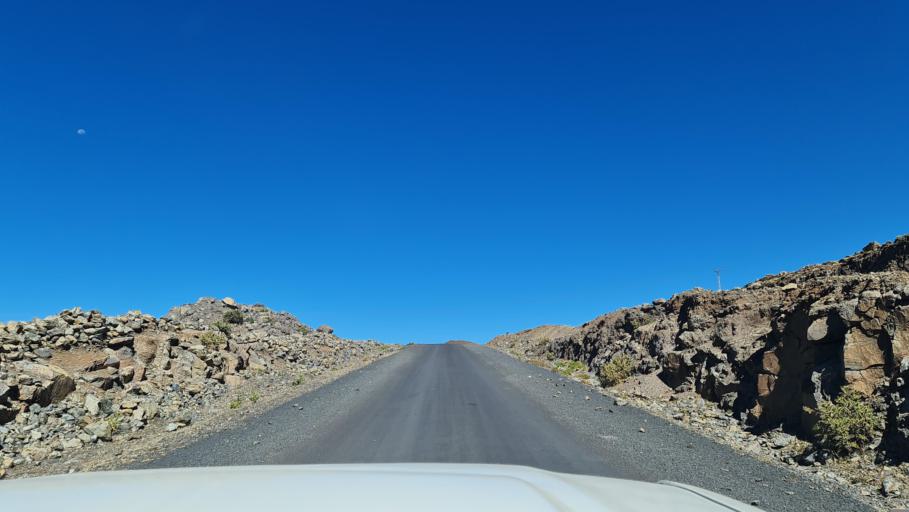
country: ET
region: Amhara
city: Debark'
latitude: 13.1534
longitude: 38.1874
